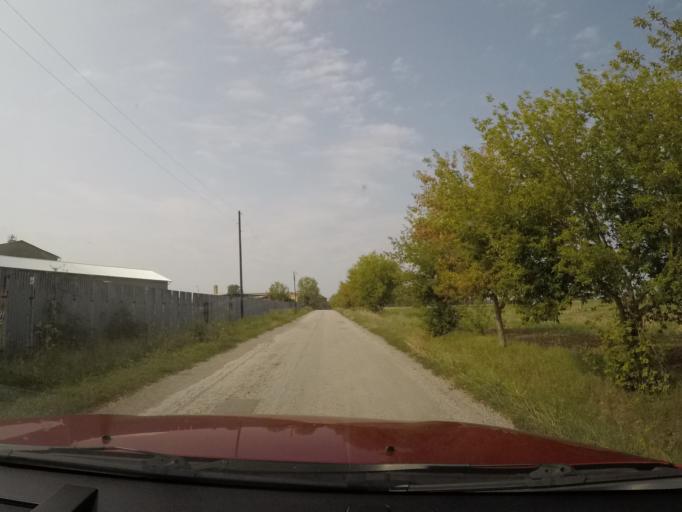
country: SK
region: Kosicky
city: Moldava nad Bodvou
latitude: 48.5891
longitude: 21.0163
